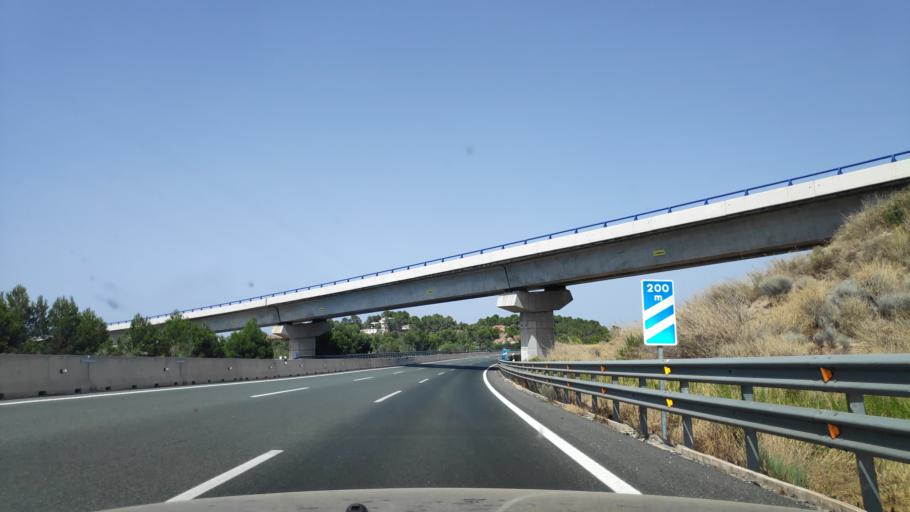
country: ES
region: Murcia
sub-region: Murcia
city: Alcantarilla
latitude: 37.9180
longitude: -1.1637
